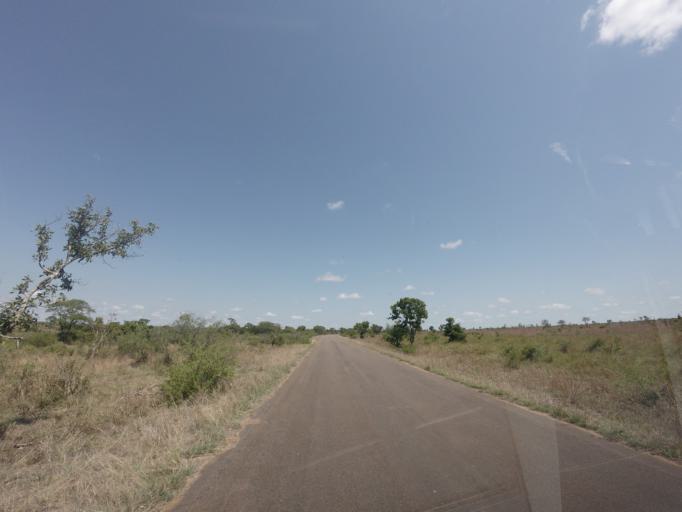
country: ZA
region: Mpumalanga
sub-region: Ehlanzeni District
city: Komatipoort
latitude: -24.9926
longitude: 31.9080
